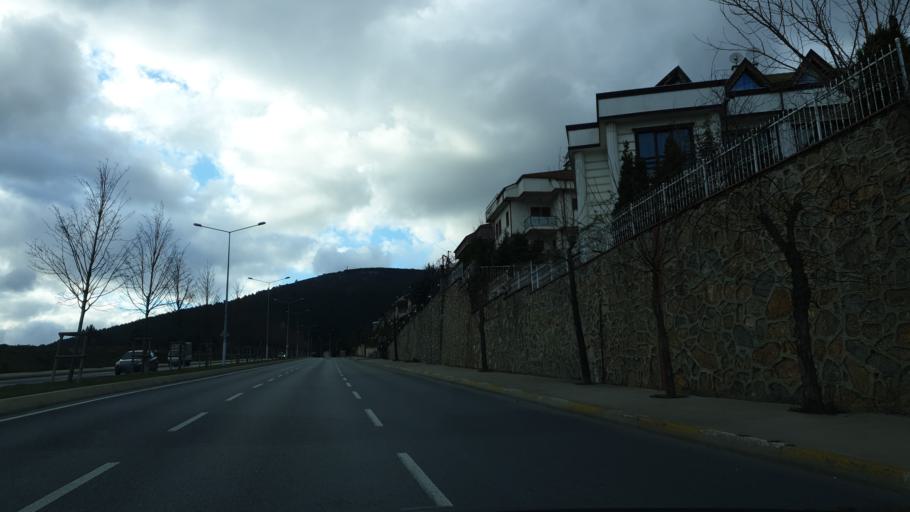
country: TR
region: Istanbul
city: Sultanbeyli
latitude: 40.9218
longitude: 29.2687
